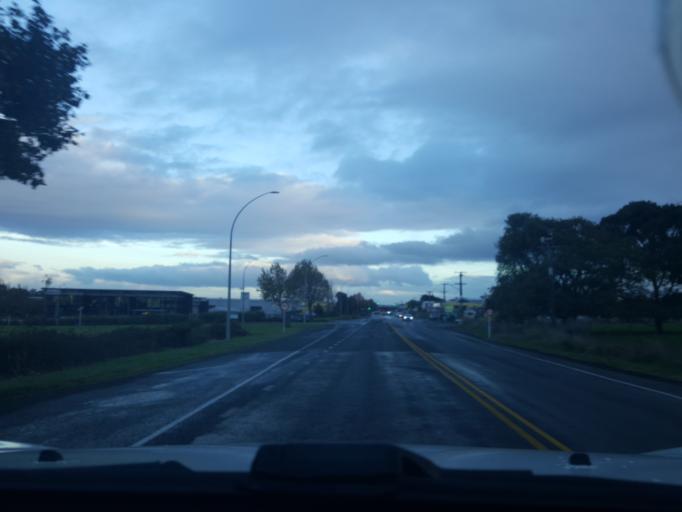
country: NZ
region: Waikato
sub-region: Waikato District
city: Ngaruawahia
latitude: -37.7259
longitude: 175.2183
